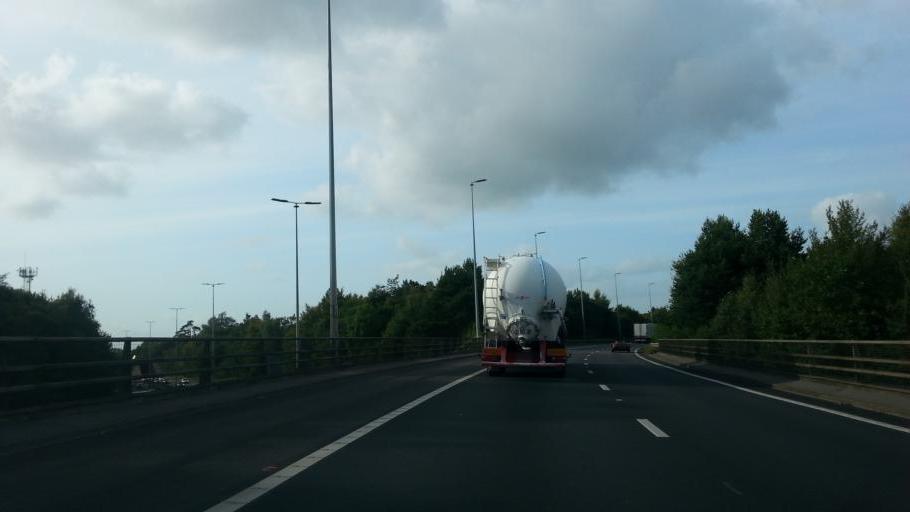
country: GB
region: England
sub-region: Southampton
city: Southampton
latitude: 50.9508
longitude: -1.3996
